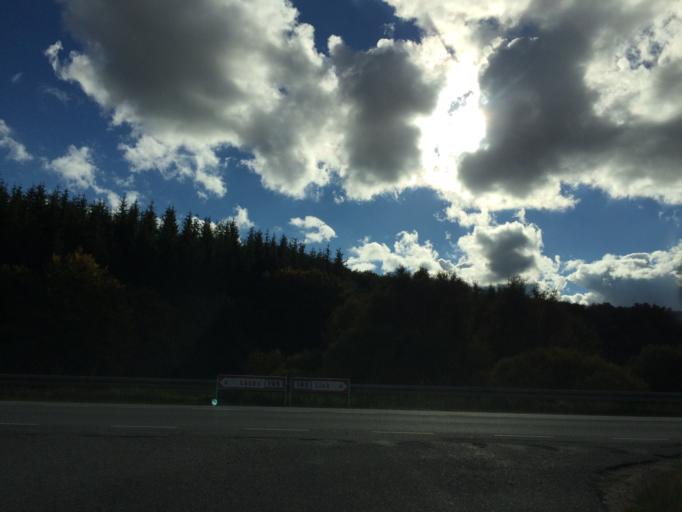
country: DK
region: Central Jutland
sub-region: Skanderborg Kommune
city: Ry
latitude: 56.1530
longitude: 9.7547
